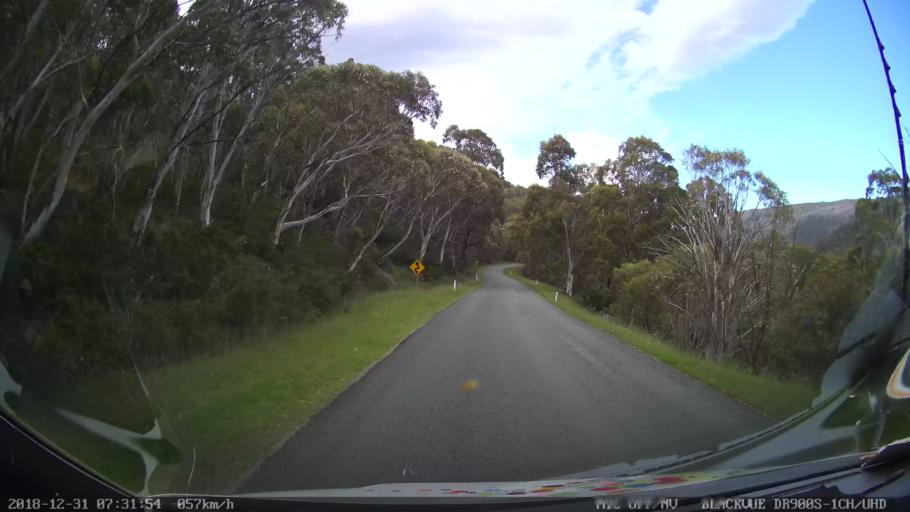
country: AU
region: New South Wales
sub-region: Snowy River
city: Jindabyne
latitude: -36.3284
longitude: 148.4695
